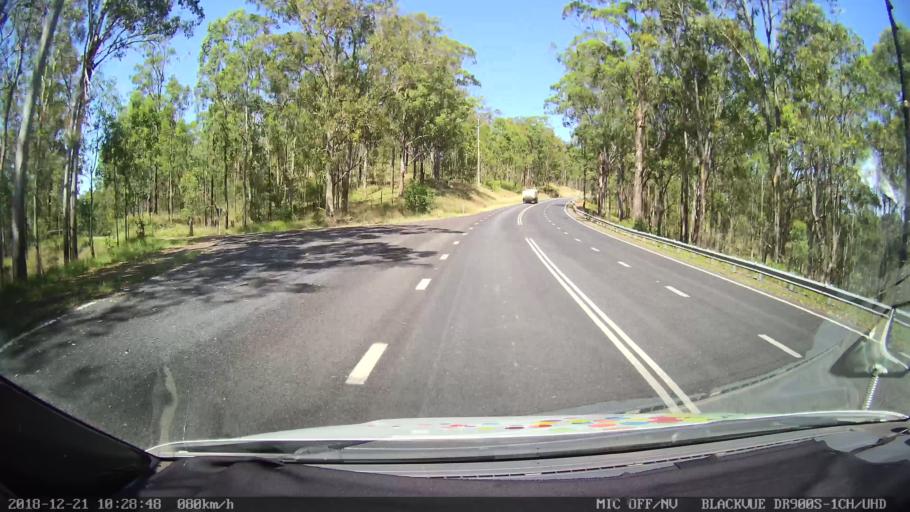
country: AU
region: New South Wales
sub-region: Clarence Valley
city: South Grafton
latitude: -29.6327
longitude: 152.7311
